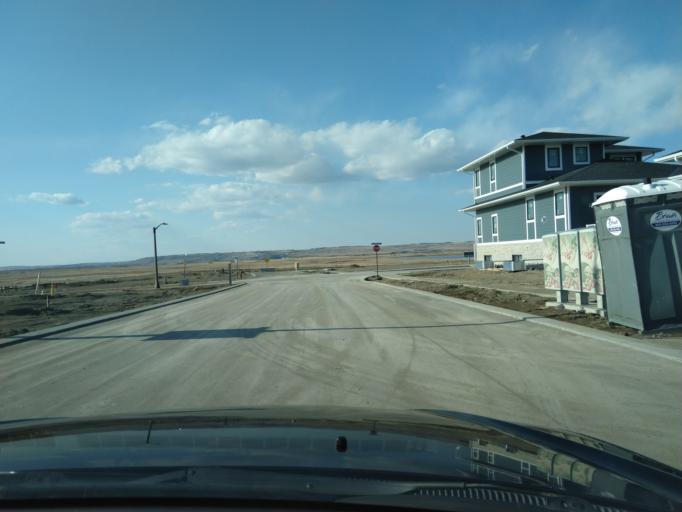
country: CA
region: Alberta
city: Cochrane
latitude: 51.1118
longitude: -114.4085
